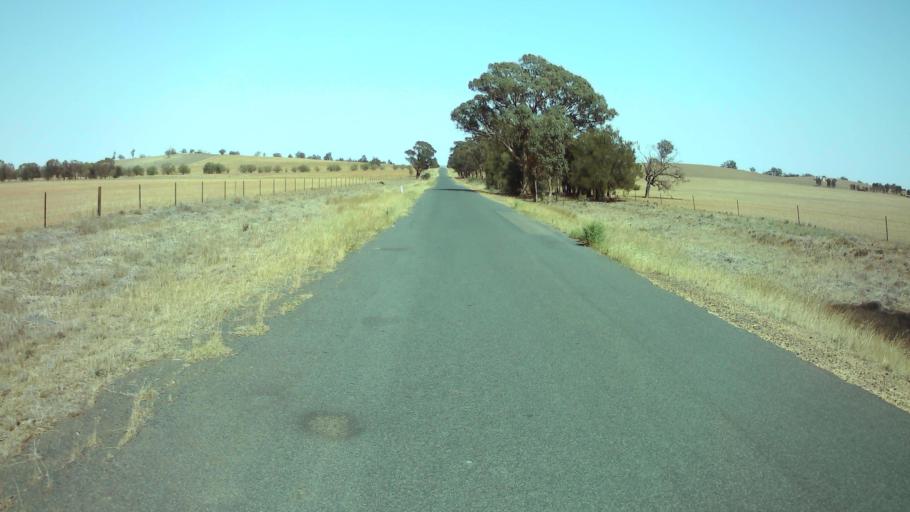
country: AU
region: New South Wales
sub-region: Weddin
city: Grenfell
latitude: -33.8570
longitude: 147.9528
